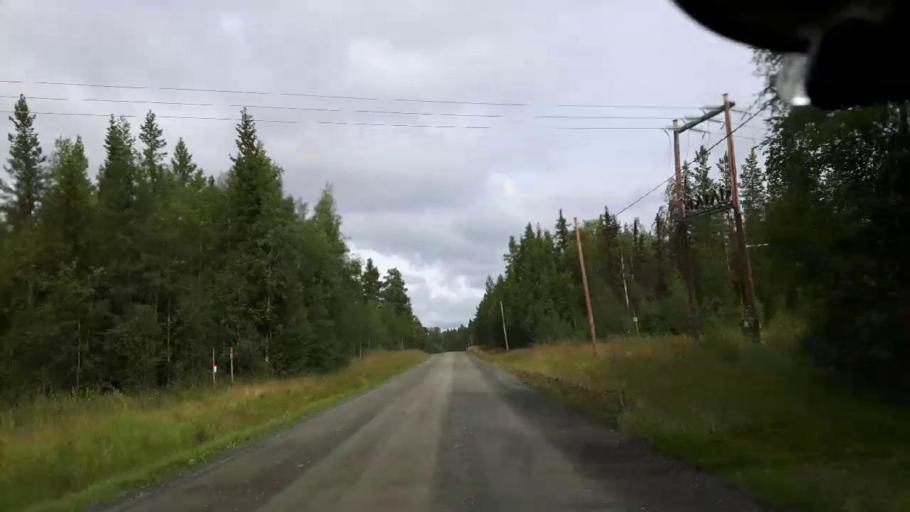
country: SE
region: Jaemtland
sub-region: Krokoms Kommun
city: Valla
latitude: 63.4030
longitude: 14.0939
